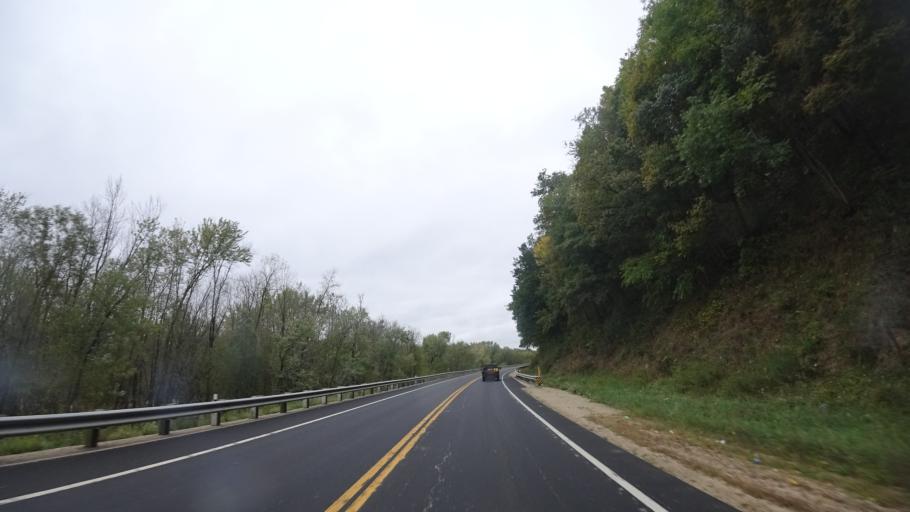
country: US
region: Wisconsin
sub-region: Grant County
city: Boscobel
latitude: 43.1420
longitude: -90.7349
